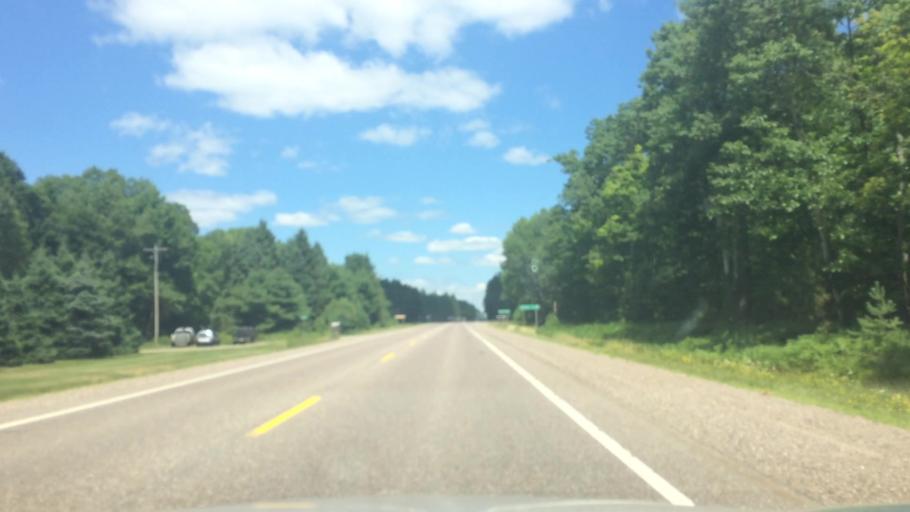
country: US
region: Wisconsin
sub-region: Vilas County
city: Lac du Flambeau
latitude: 45.9794
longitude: -89.6989
